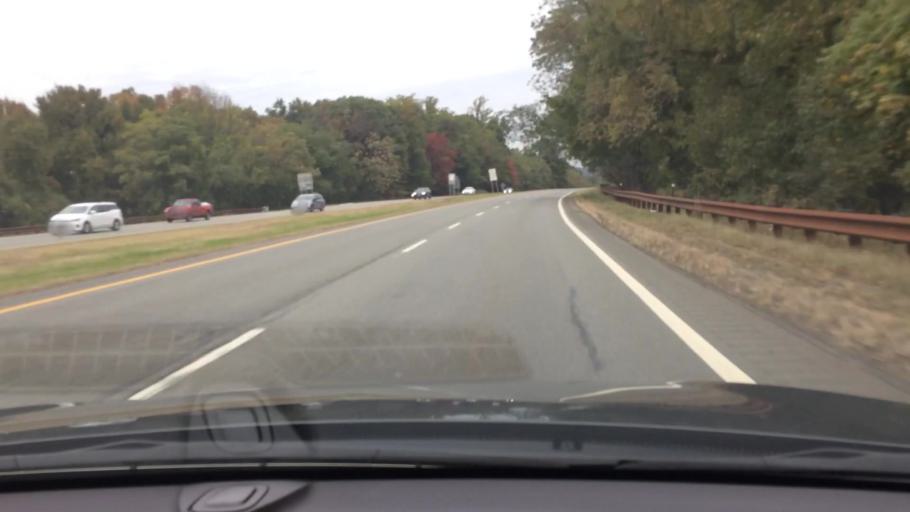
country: US
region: New York
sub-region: Westchester County
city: Hastings-on-Hudson
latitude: 40.9923
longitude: -73.9133
